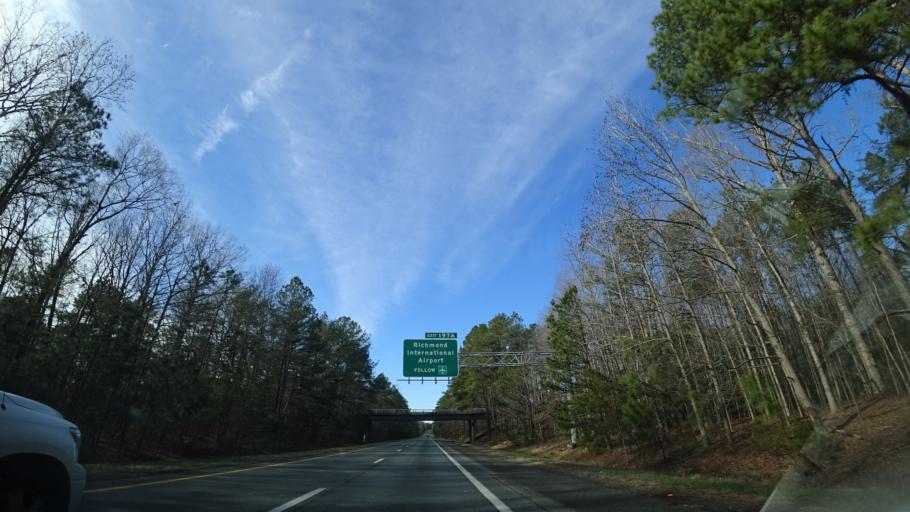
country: US
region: Virginia
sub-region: New Kent County
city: New Kent
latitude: 37.5082
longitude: -77.1243
